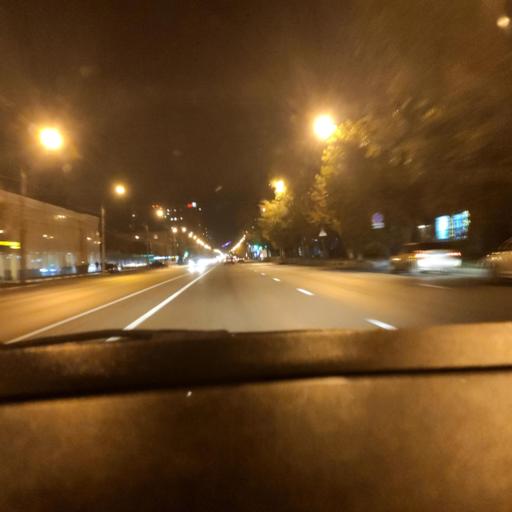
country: RU
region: Voronezj
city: Voronezh
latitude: 51.6719
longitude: 39.1570
